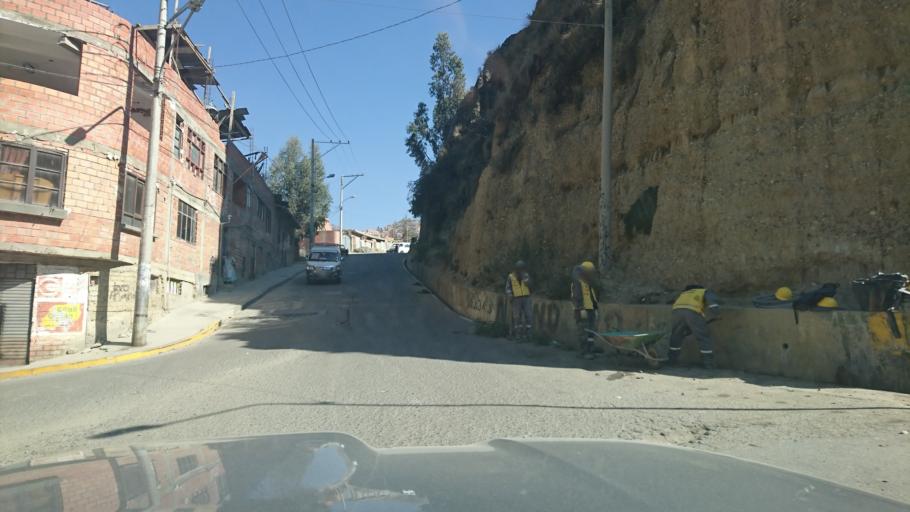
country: BO
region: La Paz
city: La Paz
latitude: -16.4801
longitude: -68.1138
